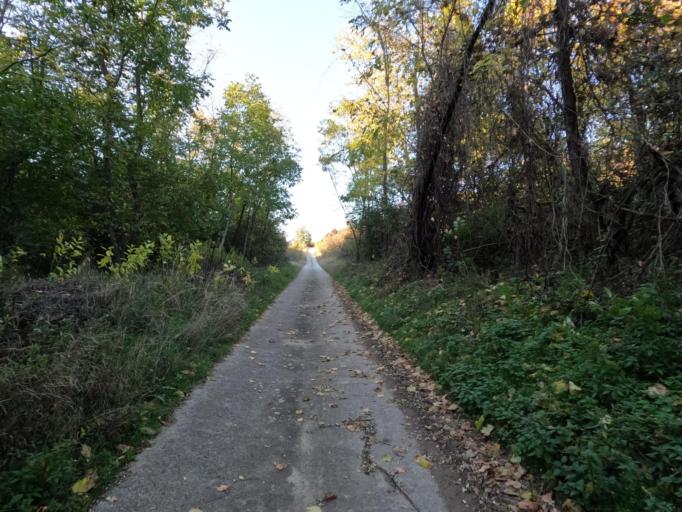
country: HU
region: Tolna
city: Szekszard
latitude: 46.3049
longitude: 18.6612
